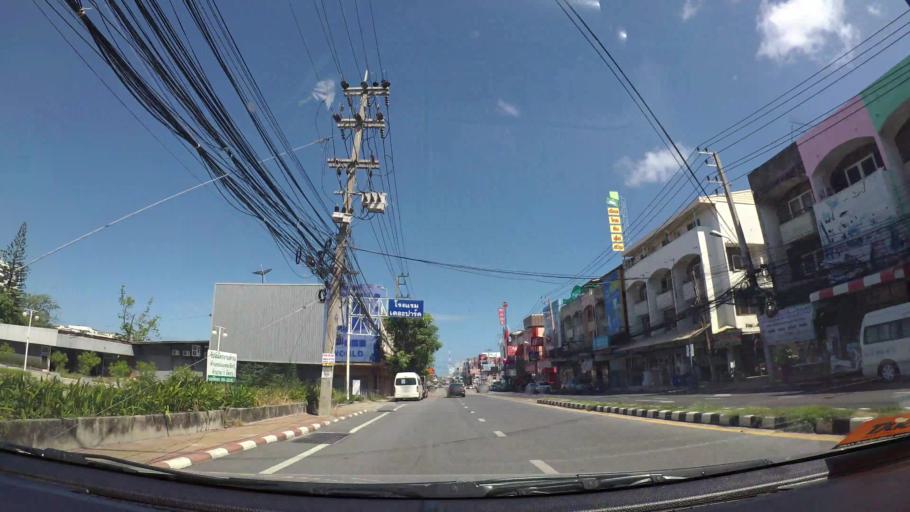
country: TH
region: Chon Buri
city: Phatthaya
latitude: 12.9321
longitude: 100.8997
